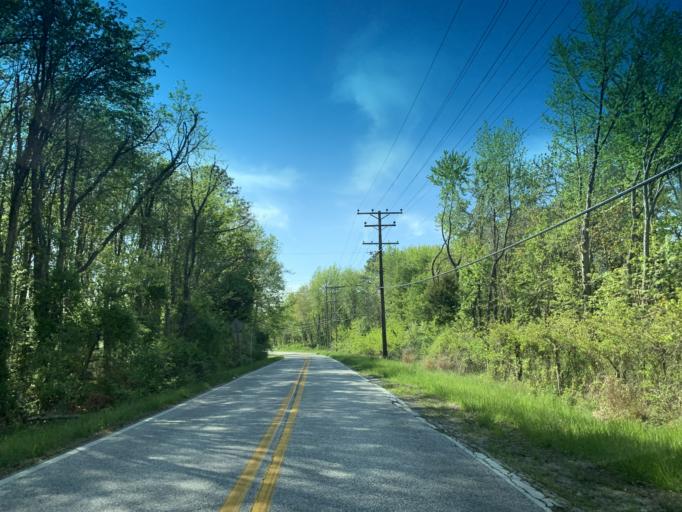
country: US
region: Maryland
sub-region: Anne Arundel County
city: Cape Saint Claire
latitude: 39.0183
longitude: -76.4130
